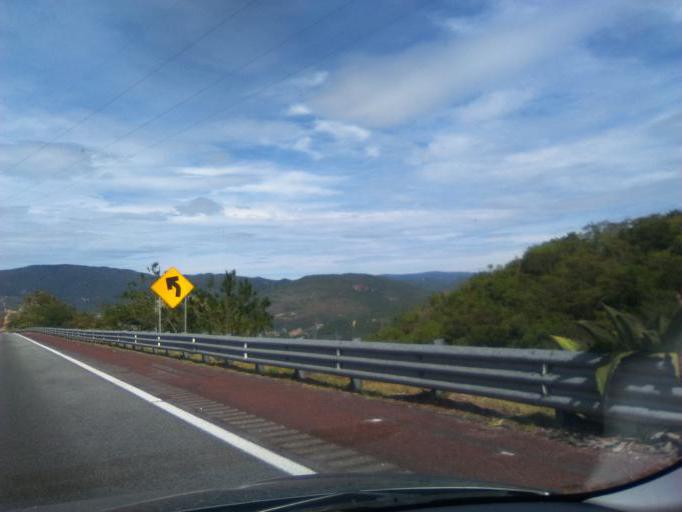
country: MX
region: Guerrero
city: Mazatlan
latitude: 17.4599
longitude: -99.4755
